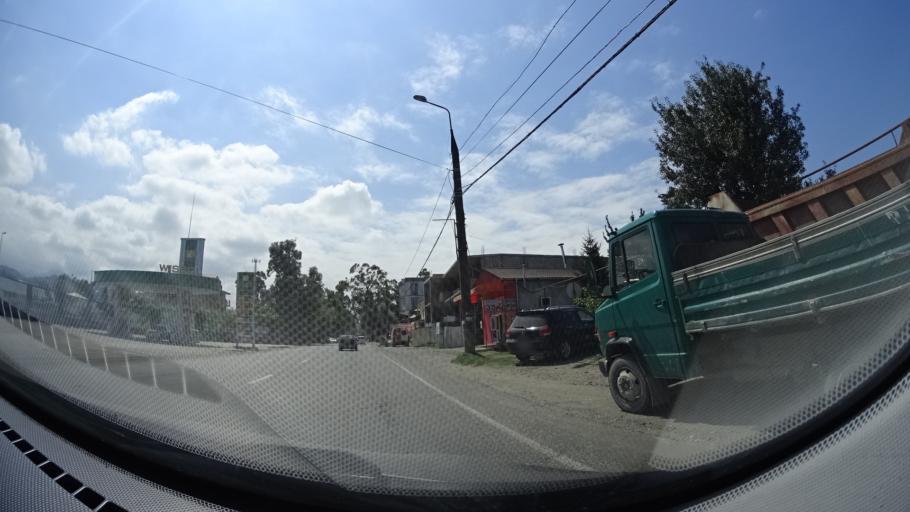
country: GE
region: Ajaria
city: Batumi
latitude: 41.6171
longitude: 41.6194
